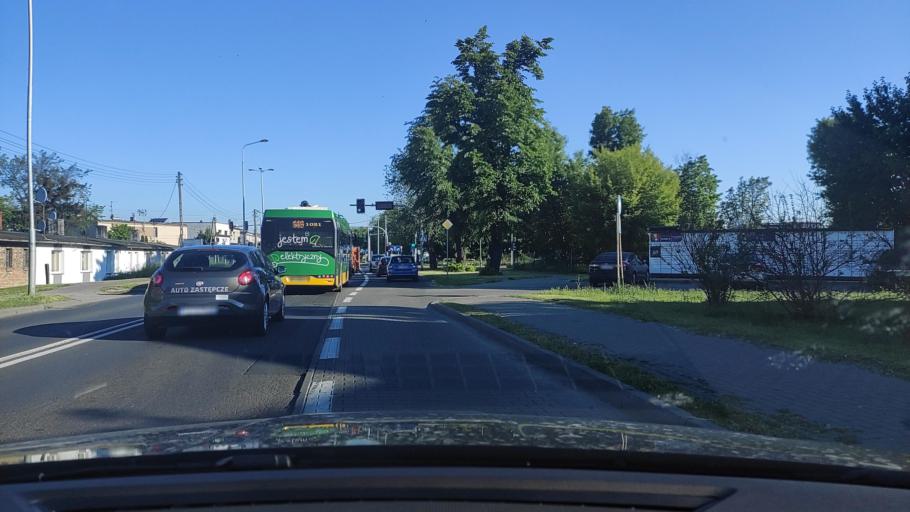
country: PL
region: Greater Poland Voivodeship
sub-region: Powiat poznanski
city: Lubon
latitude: 52.3731
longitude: 16.8949
